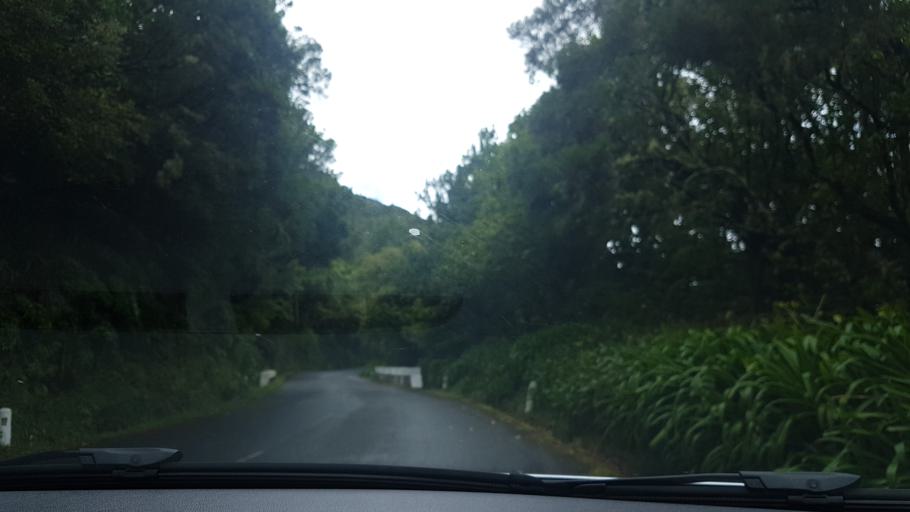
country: PT
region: Madeira
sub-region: Sao Vicente
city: Sao Vicente
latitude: 32.7547
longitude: -17.0148
